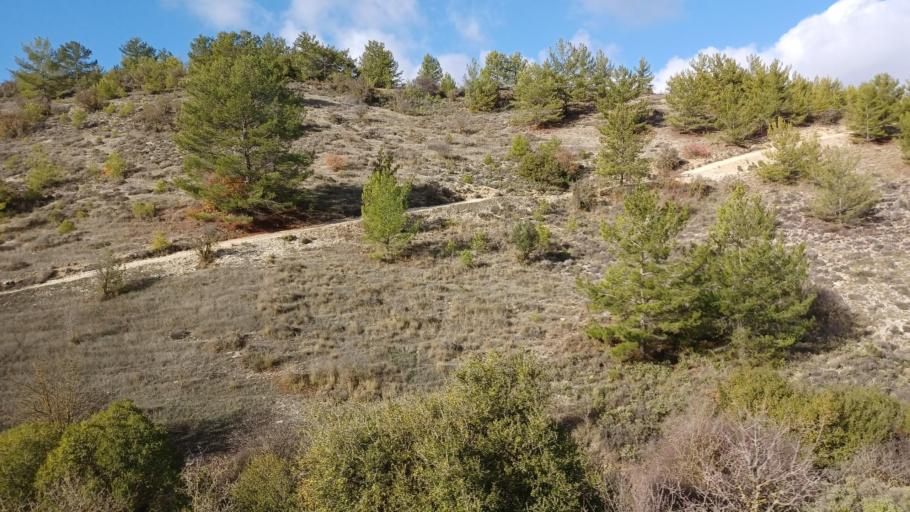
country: CY
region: Limassol
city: Pachna
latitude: 34.8478
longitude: 32.6869
